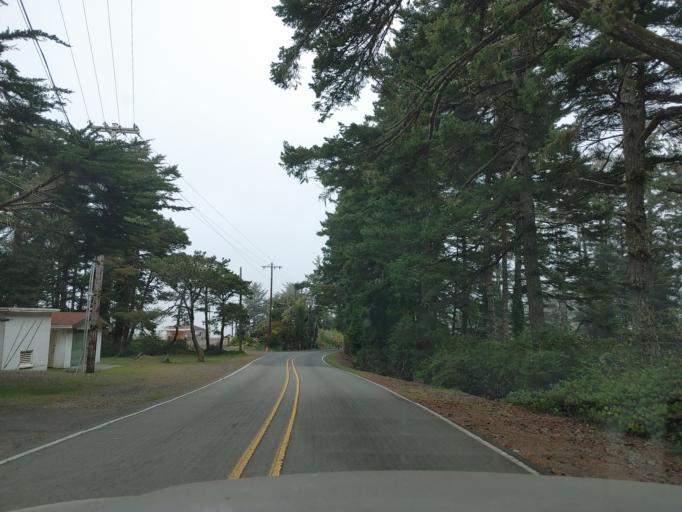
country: US
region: Oregon
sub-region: Coos County
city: Lakeside
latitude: 43.6640
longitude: -124.1977
